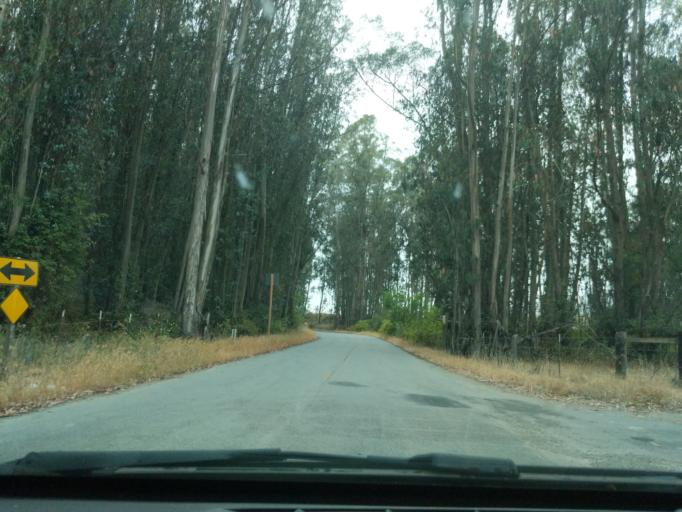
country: US
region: California
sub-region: San Benito County
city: Aromas
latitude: 36.8926
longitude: -121.6046
